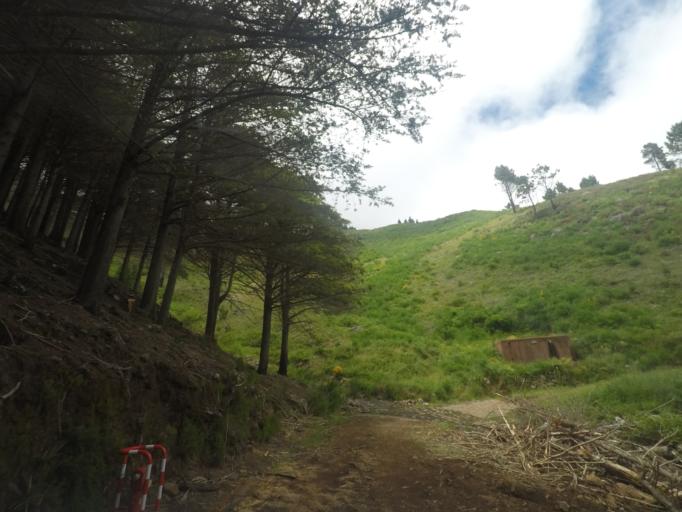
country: PT
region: Madeira
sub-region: Funchal
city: Nossa Senhora do Monte
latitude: 32.7063
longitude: -16.9042
